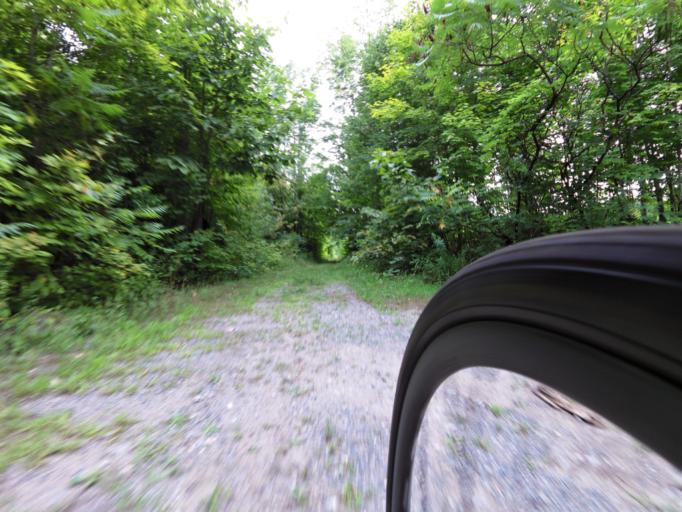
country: CA
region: Ontario
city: Perth
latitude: 44.6178
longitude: -76.2564
